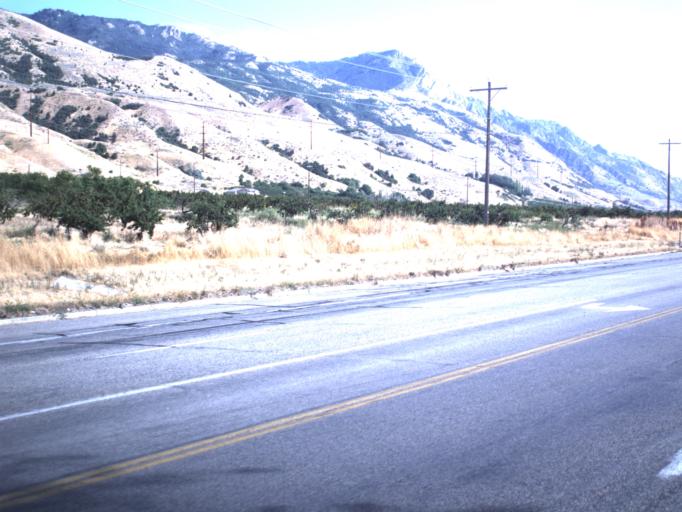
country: US
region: Utah
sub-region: Box Elder County
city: Perry
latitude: 41.4553
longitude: -112.0388
